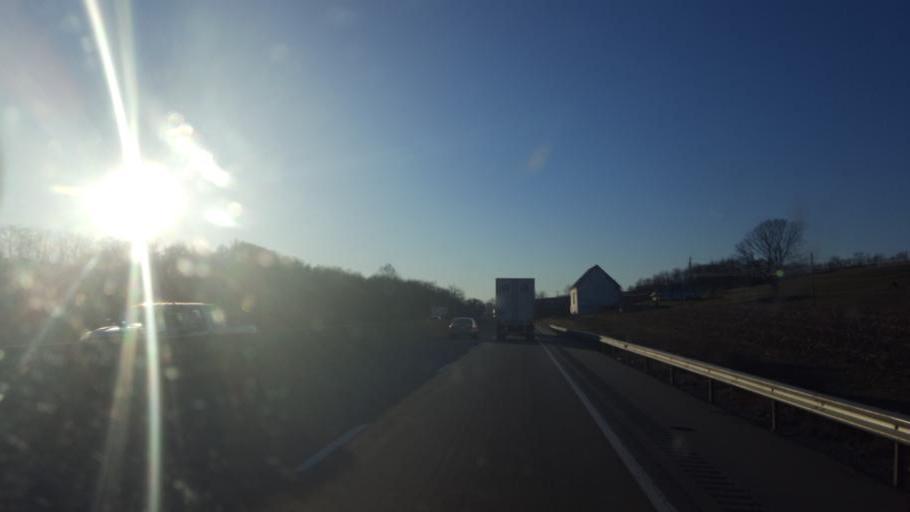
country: US
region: Pennsylvania
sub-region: Washington County
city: Ellsworth
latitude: 40.1586
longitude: -80.0447
